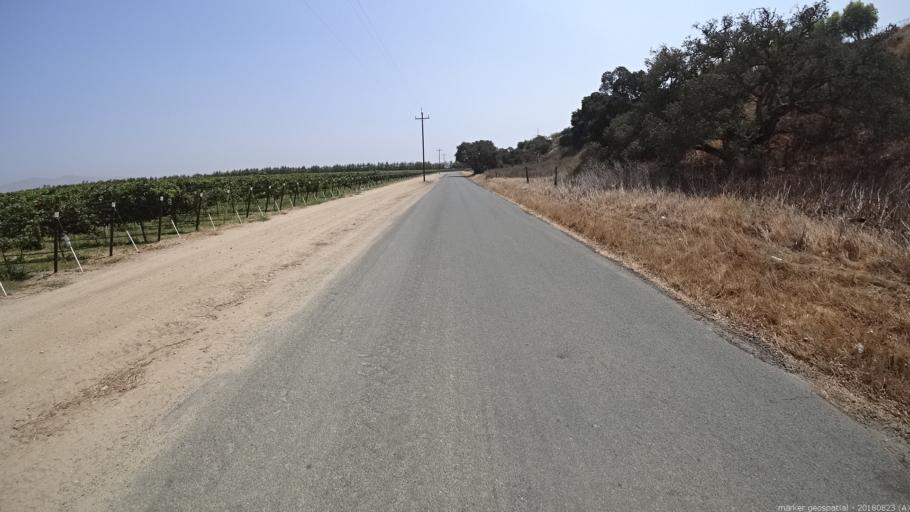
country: US
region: California
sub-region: Monterey County
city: Soledad
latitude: 36.3691
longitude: -121.3152
